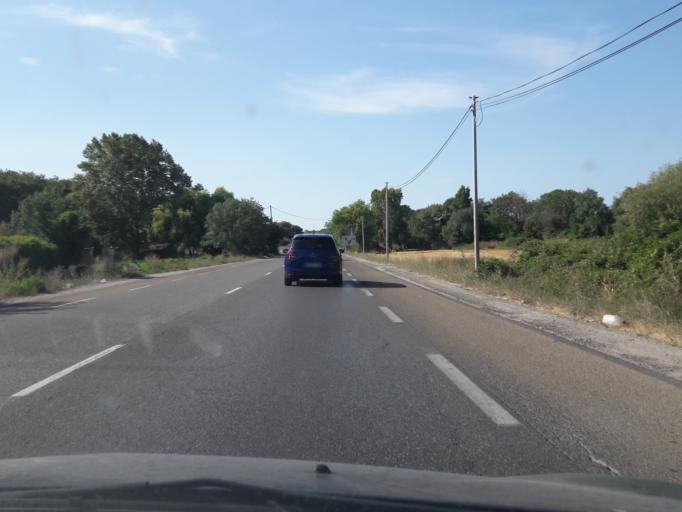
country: FR
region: Provence-Alpes-Cote d'Azur
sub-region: Departement des Bouches-du-Rhone
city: Bouc-Bel-Air
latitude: 43.4873
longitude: 5.4099
